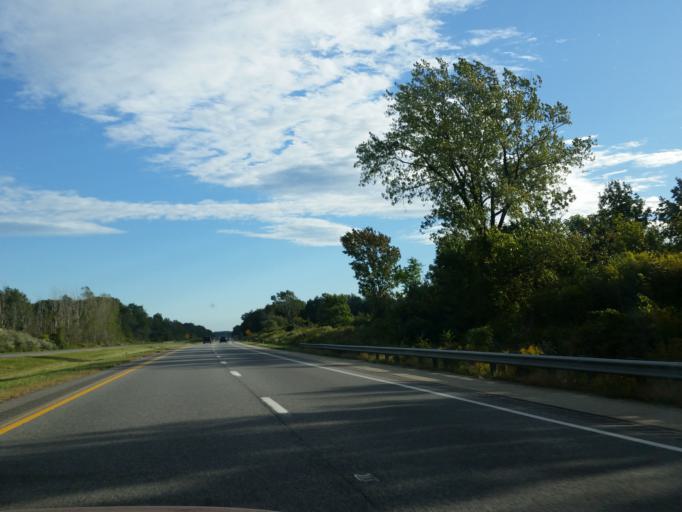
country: US
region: Pennsylvania
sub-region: Erie County
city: North East
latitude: 42.2015
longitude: -79.8141
